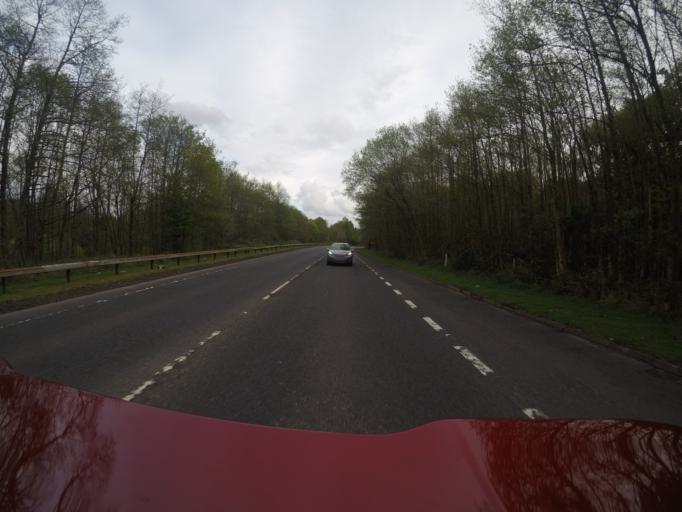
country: GB
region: Scotland
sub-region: West Dunbartonshire
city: Balloch
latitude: 56.0889
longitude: -4.6411
